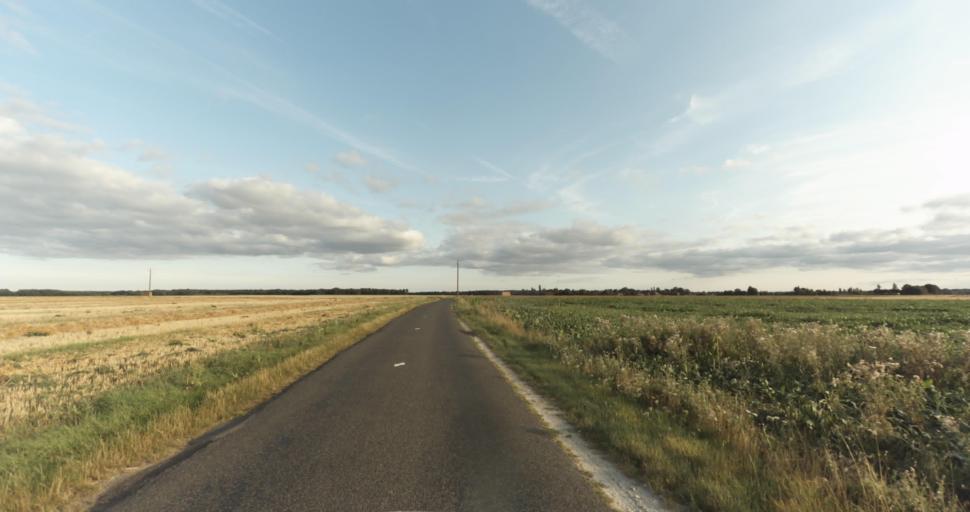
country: FR
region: Haute-Normandie
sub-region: Departement de l'Eure
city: Marcilly-sur-Eure
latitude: 48.8278
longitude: 1.2872
